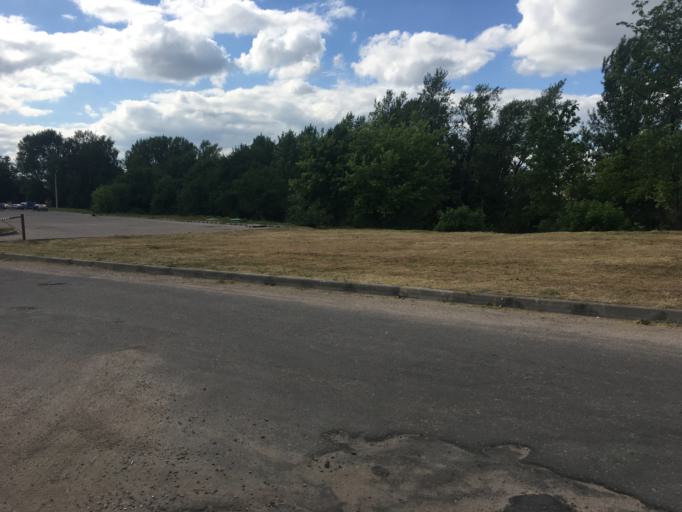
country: BY
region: Grodnenskaya
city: Hrodna
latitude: 53.7141
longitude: 23.8165
